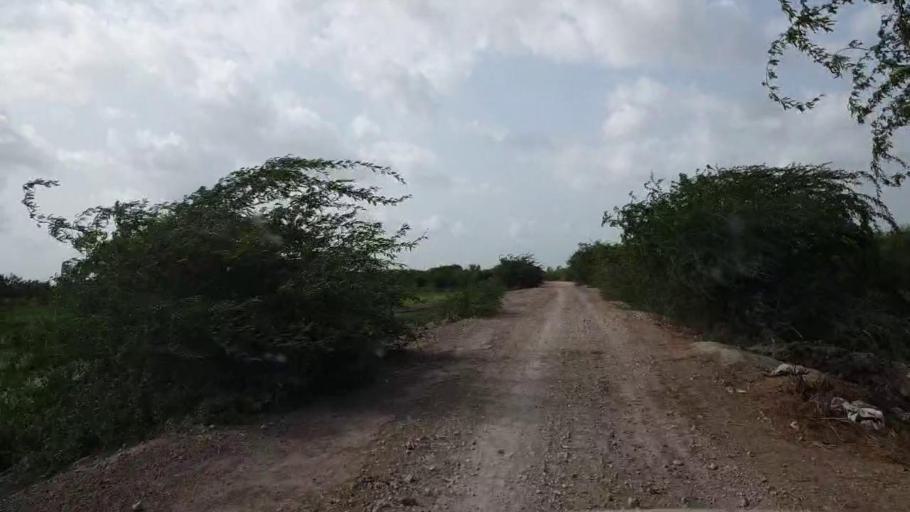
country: PK
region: Sindh
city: Kario
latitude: 24.6955
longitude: 68.6486
